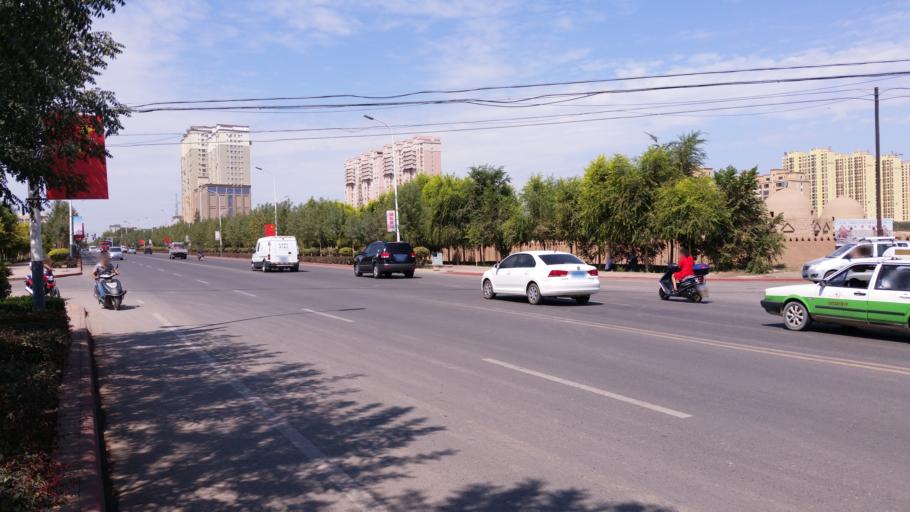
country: CN
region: Xinjiang Uygur Zizhiqu
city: Laochenglu
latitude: 42.9500
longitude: 89.1987
